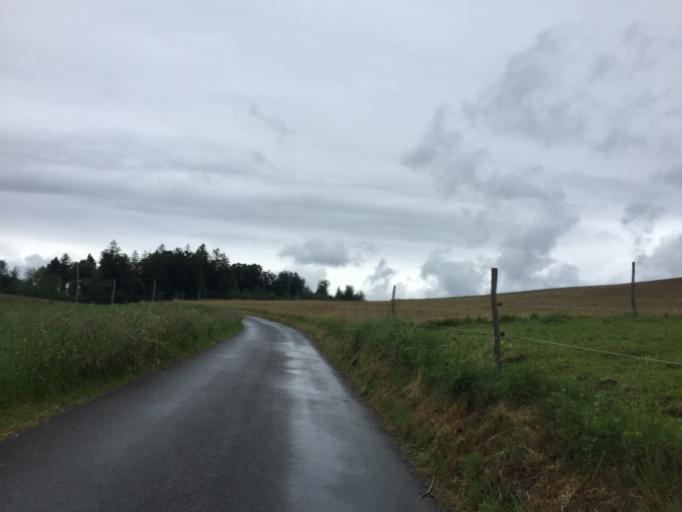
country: CH
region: Bern
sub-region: Bern-Mittelland District
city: Taegertschi
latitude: 46.8877
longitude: 7.5806
